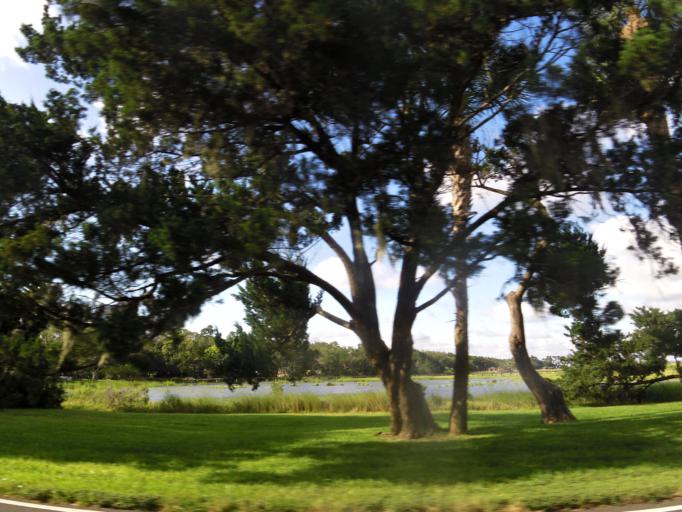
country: US
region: Georgia
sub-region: Glynn County
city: Saint Simons Island
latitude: 31.1824
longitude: -81.3700
